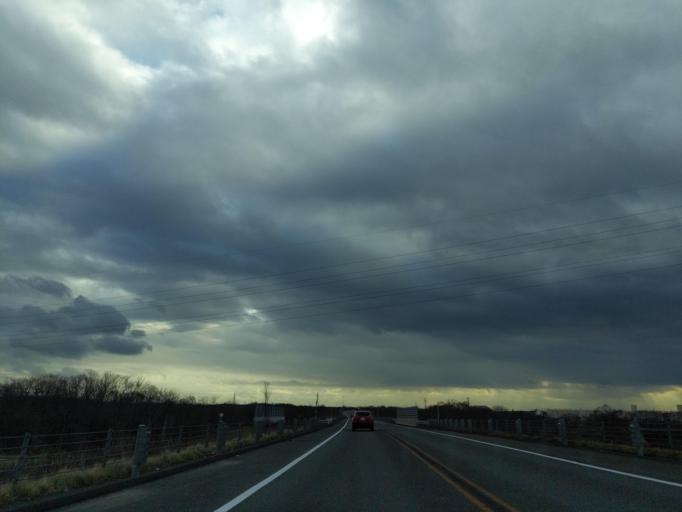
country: JP
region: Hokkaido
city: Chitose
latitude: 42.8382
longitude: 141.6929
